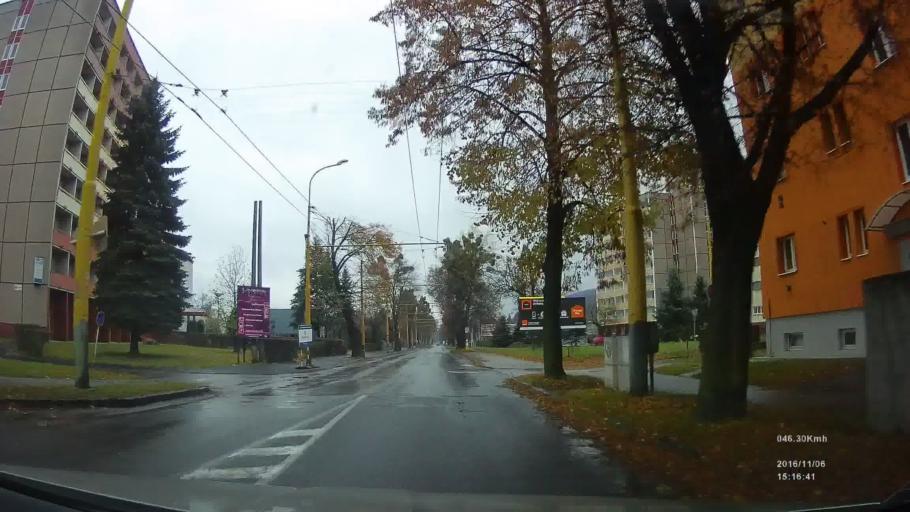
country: SK
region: Presovsky
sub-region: Okres Presov
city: Presov
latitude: 48.9860
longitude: 21.2428
